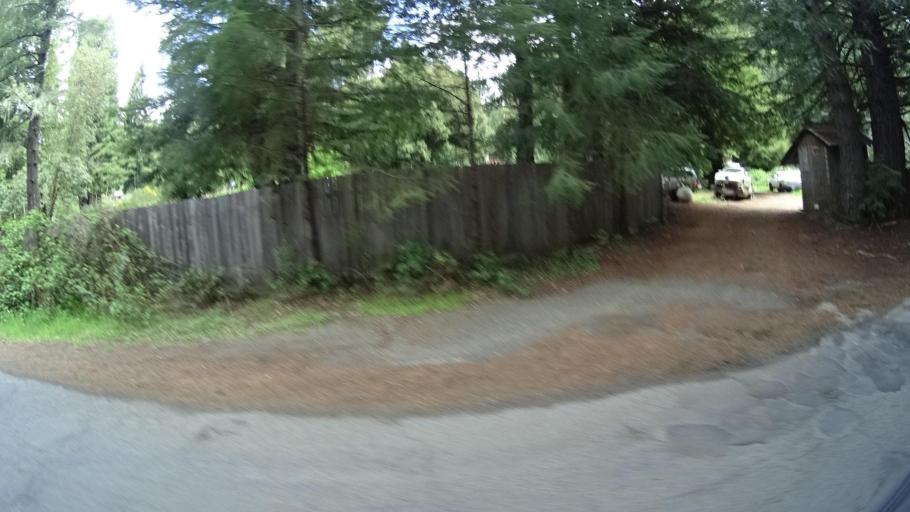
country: US
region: California
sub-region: Humboldt County
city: Redway
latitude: 40.0219
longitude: -123.9385
